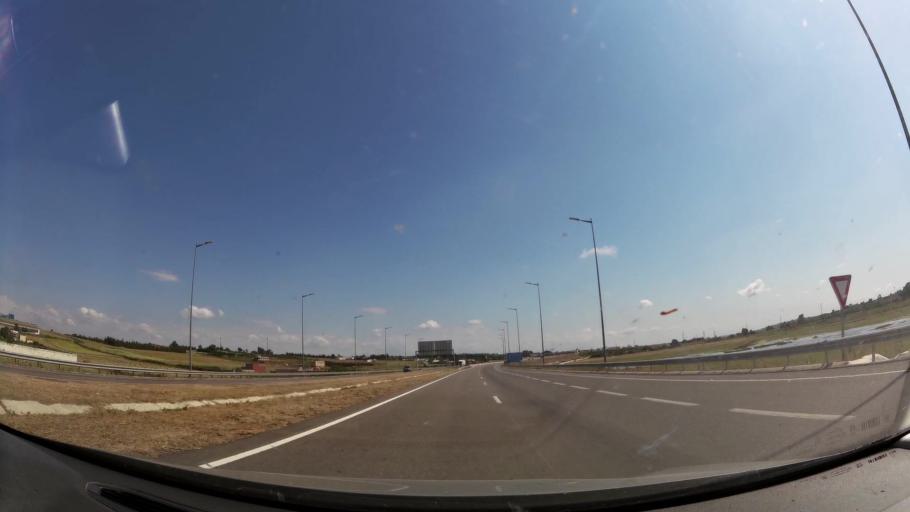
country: MA
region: Rabat-Sale-Zemmour-Zaer
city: Sale
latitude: 33.9726
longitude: -6.7392
